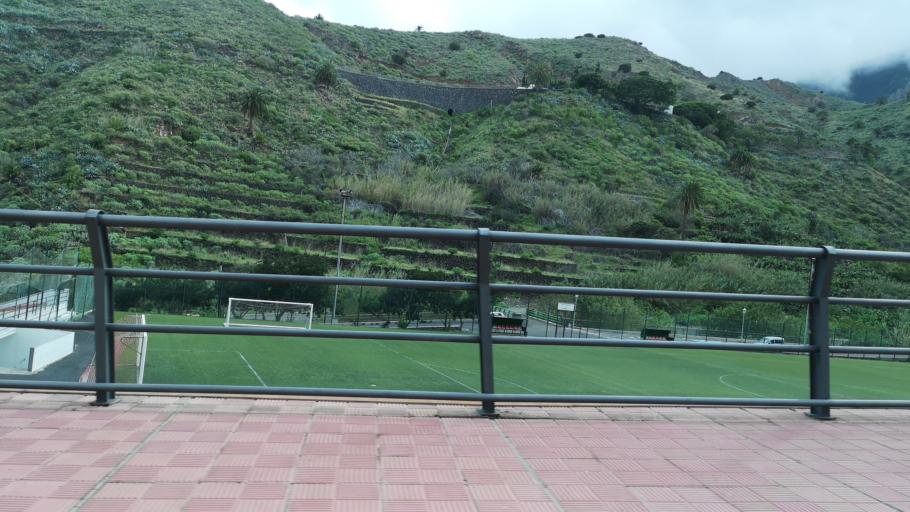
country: ES
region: Canary Islands
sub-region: Provincia de Santa Cruz de Tenerife
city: Hermigua
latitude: 28.1635
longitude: -17.1983
